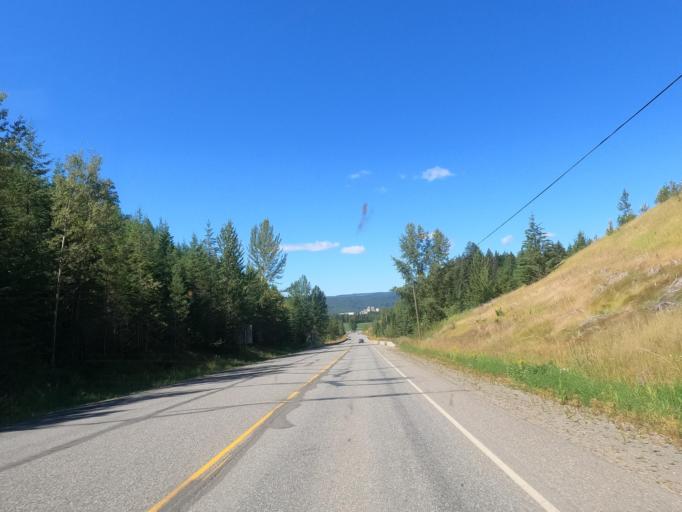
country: CA
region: British Columbia
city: Quesnel
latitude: 53.0169
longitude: -122.4829
